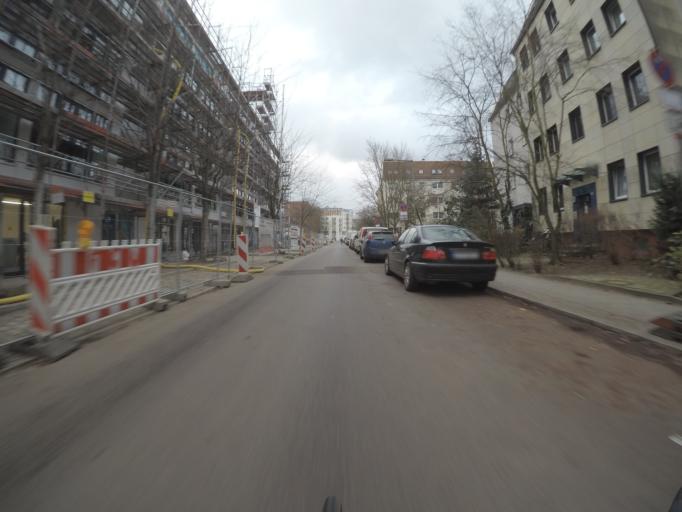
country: DE
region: Berlin
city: Berlin Koepenick
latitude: 52.4440
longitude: 13.5809
